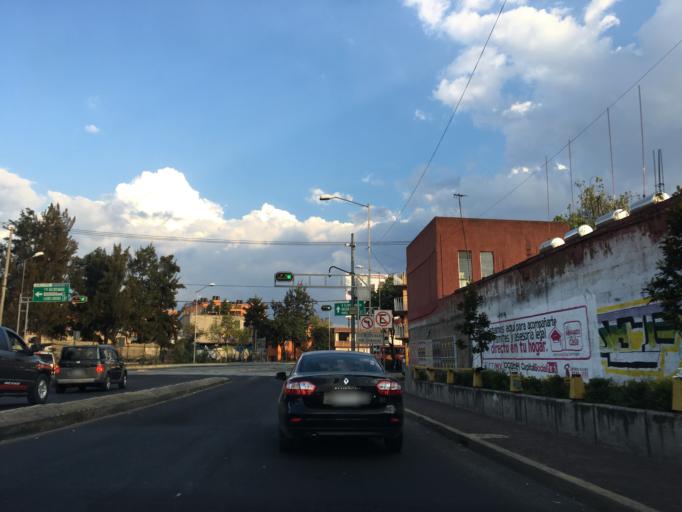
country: MX
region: Mexico City
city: Cuauhtemoc
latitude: 19.4615
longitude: -99.1445
